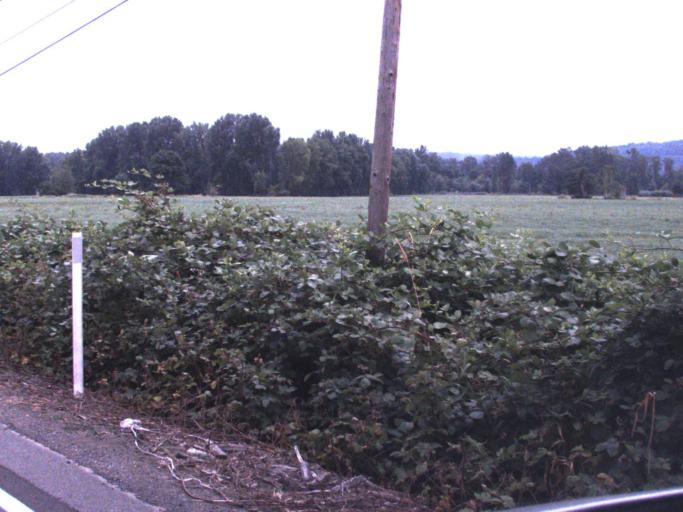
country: US
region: Washington
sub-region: King County
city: Fall City
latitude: 47.5943
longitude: -121.9102
